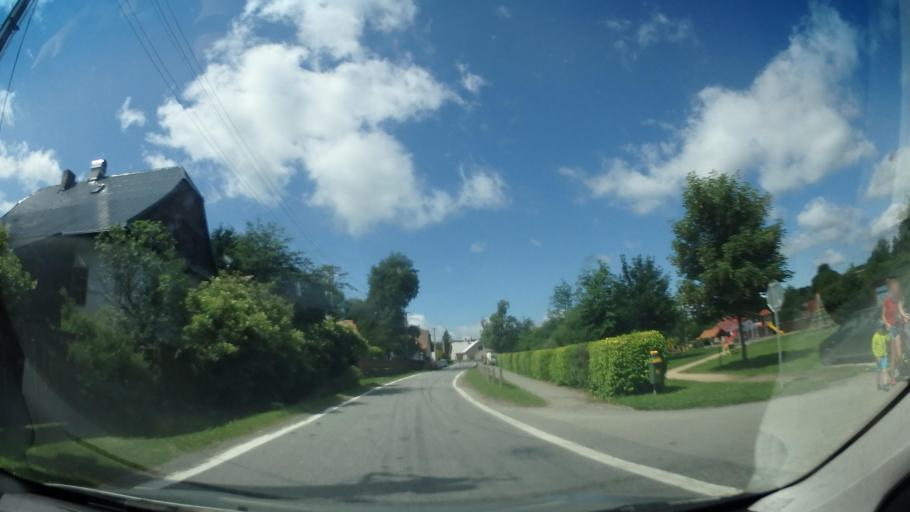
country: CZ
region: Vysocina
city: Heralec
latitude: 49.6295
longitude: 16.0407
